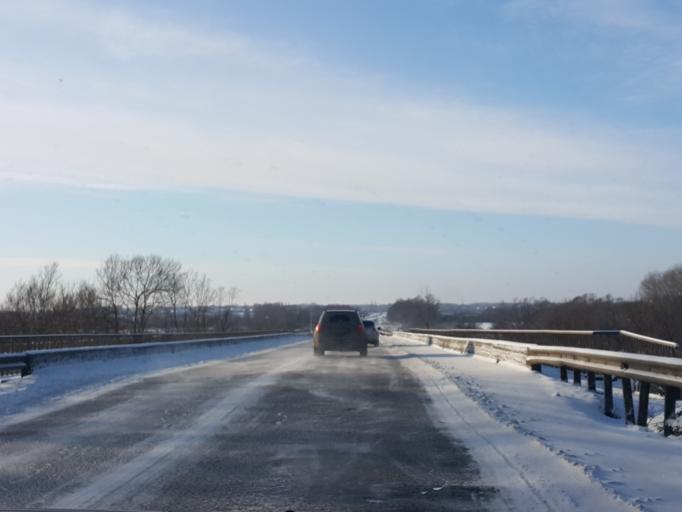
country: RU
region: Tambov
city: Znamenka
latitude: 52.4160
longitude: 41.4847
